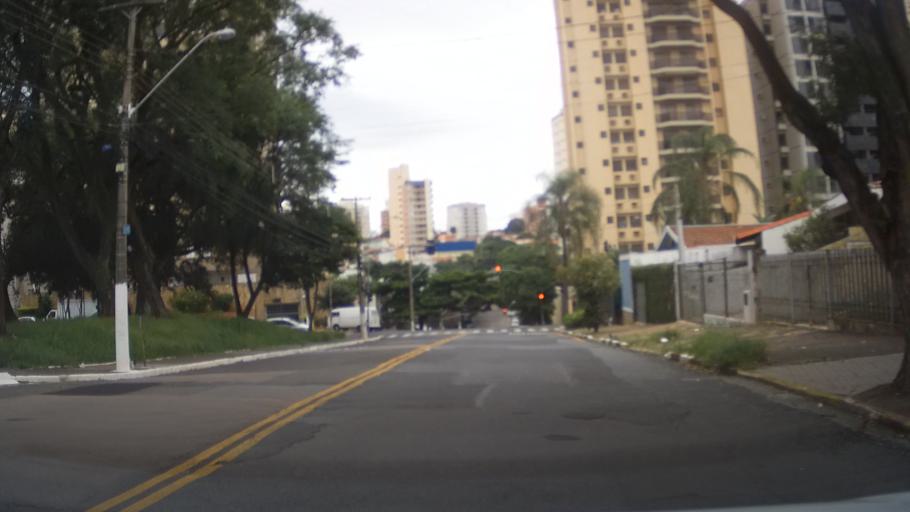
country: BR
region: Sao Paulo
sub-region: Campinas
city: Campinas
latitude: -22.9140
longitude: -47.0426
